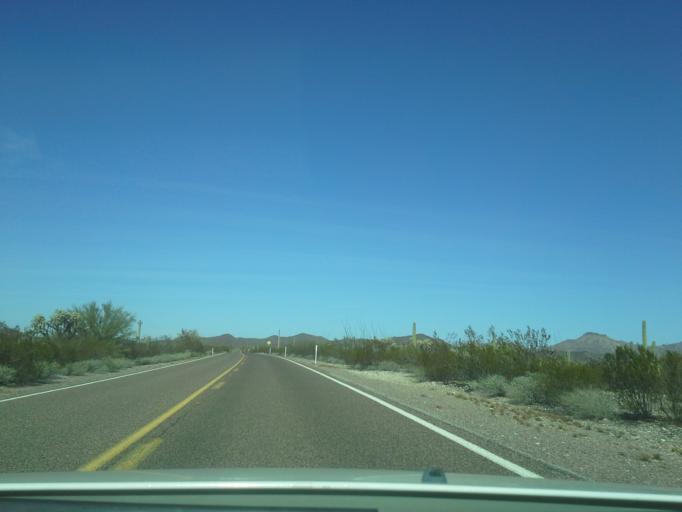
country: MX
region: Sonora
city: Sonoyta
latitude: 31.9393
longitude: -112.7987
